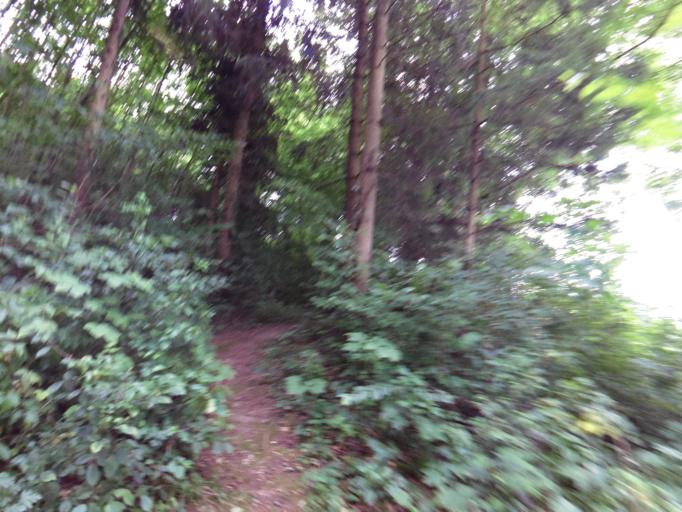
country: CH
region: Zurich
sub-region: Bezirk Zuerich
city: Zuerich (Kreis 10) / Hoengg
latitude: 47.4102
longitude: 8.4898
